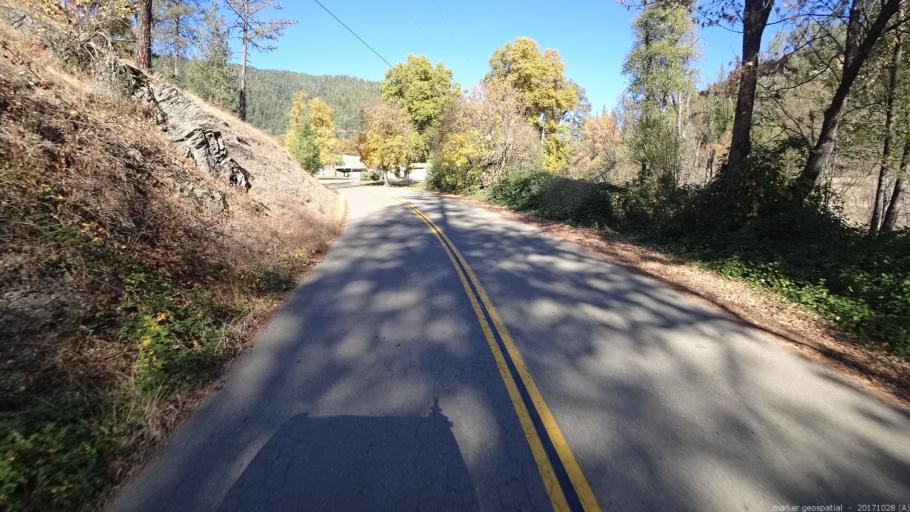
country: US
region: California
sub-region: Trinity County
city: Lewiston
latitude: 40.7881
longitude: -122.6096
